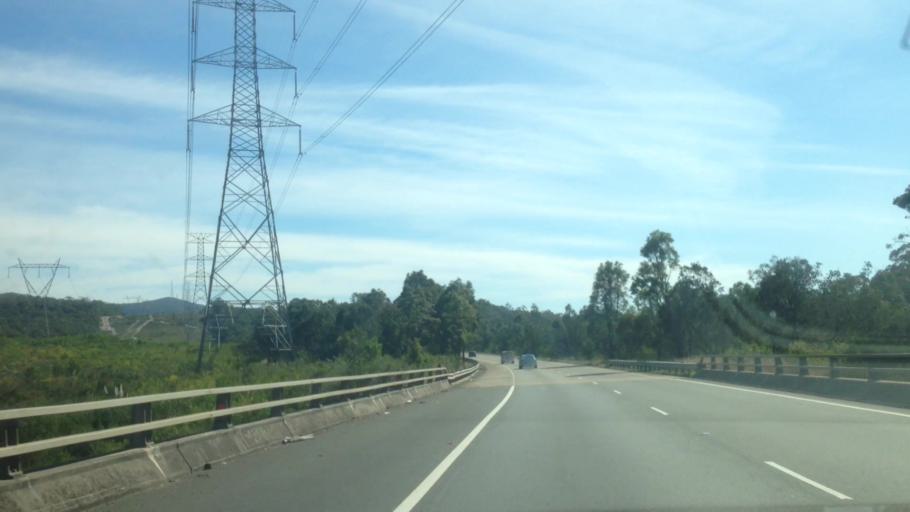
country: AU
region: New South Wales
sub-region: Lake Macquarie Shire
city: Fennell Bay
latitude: -32.9532
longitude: 151.5450
